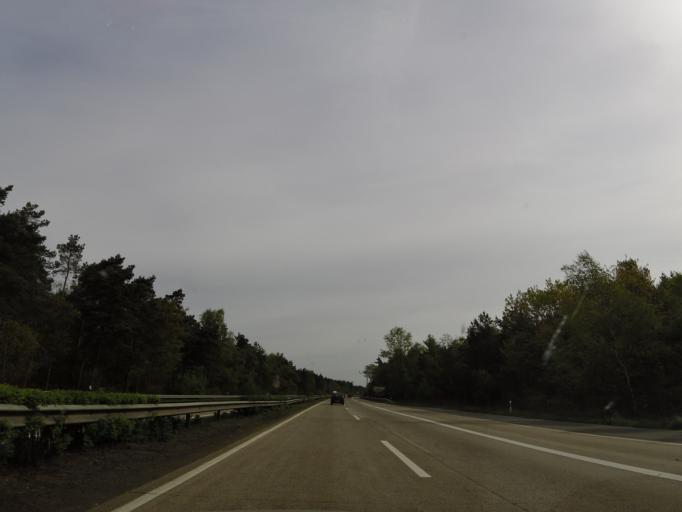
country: DE
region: Lower Saxony
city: Soltau
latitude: 52.9120
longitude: 9.7975
